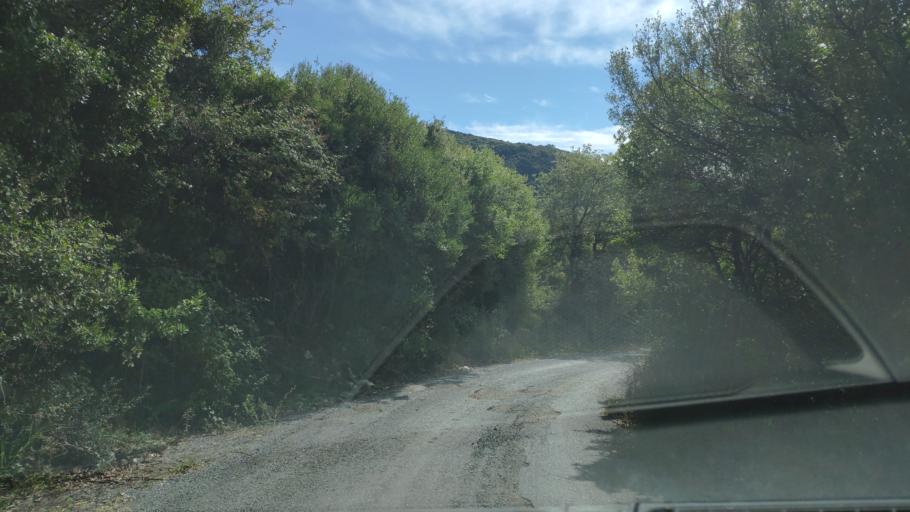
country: GR
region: Peloponnese
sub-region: Nomos Arkadias
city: Dimitsana
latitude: 37.5383
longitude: 22.0513
